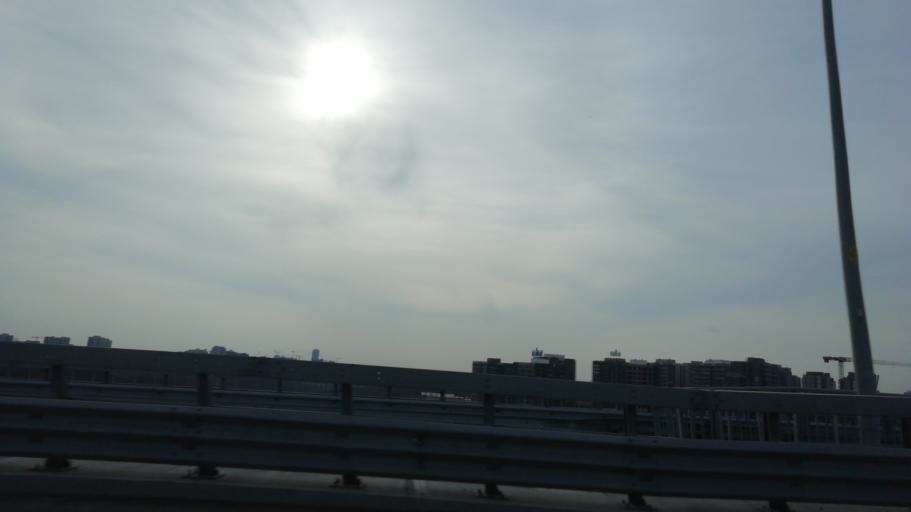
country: TR
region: Istanbul
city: Basaksehir
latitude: 41.1273
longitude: 28.7931
